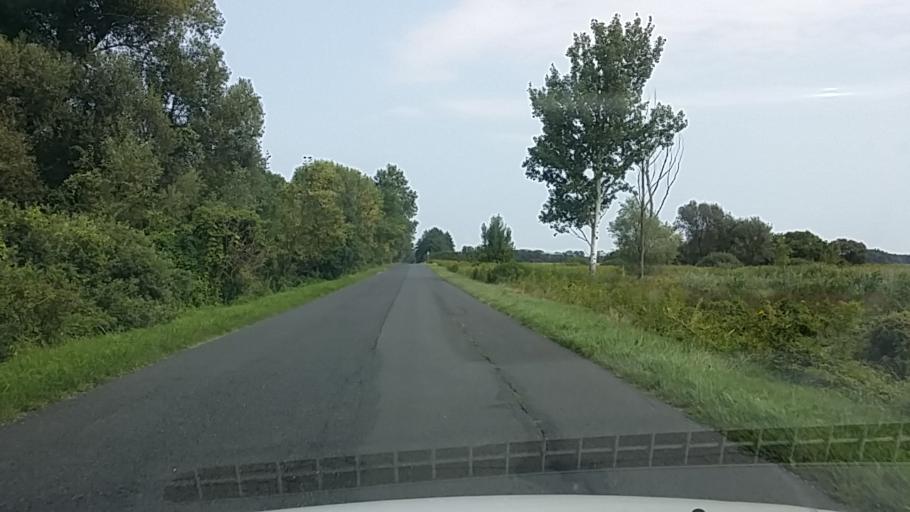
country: HU
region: Gyor-Moson-Sopron
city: Lebeny
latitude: 47.7349
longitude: 17.3341
